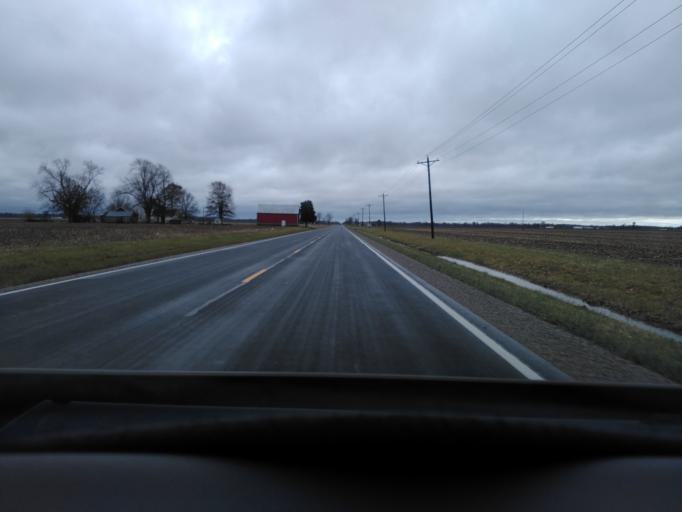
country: US
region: Illinois
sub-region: Effingham County
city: Altamont
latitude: 39.0179
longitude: -88.7484
